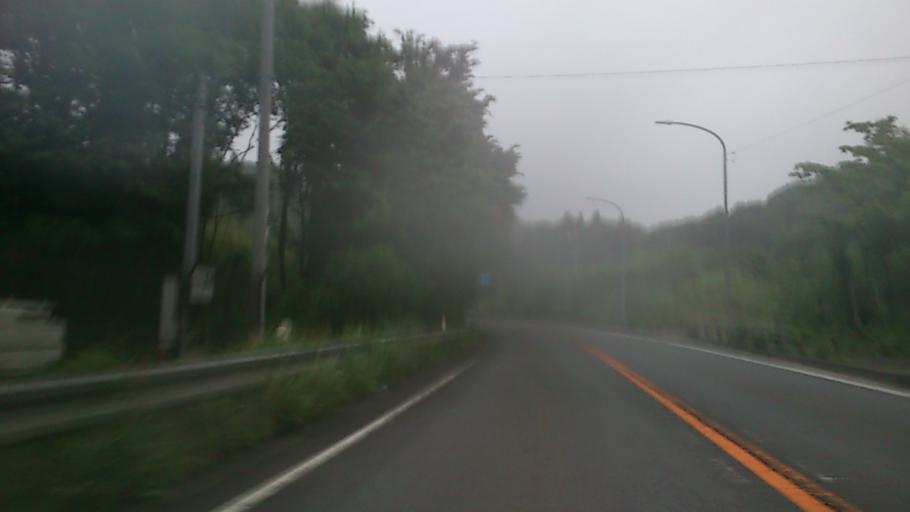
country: JP
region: Tochigi
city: Kuroiso
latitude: 37.0791
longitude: 140.1292
